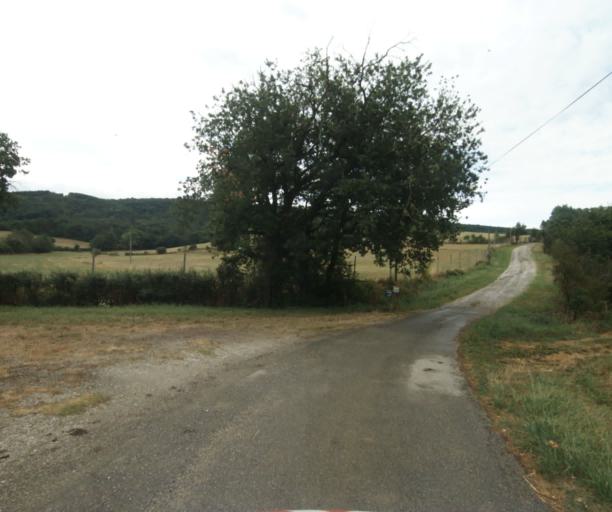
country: FR
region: Midi-Pyrenees
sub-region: Departement de la Haute-Garonne
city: Revel
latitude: 43.4250
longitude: 1.9984
